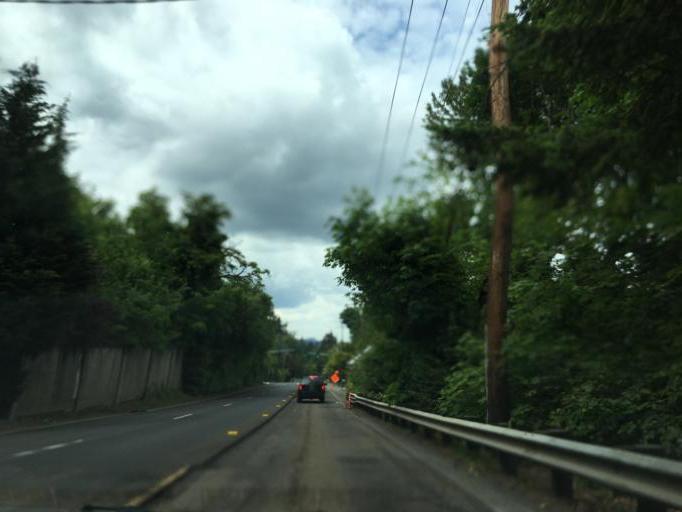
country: US
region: Oregon
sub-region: Clackamas County
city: Milwaukie
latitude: 45.4495
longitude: -122.6584
